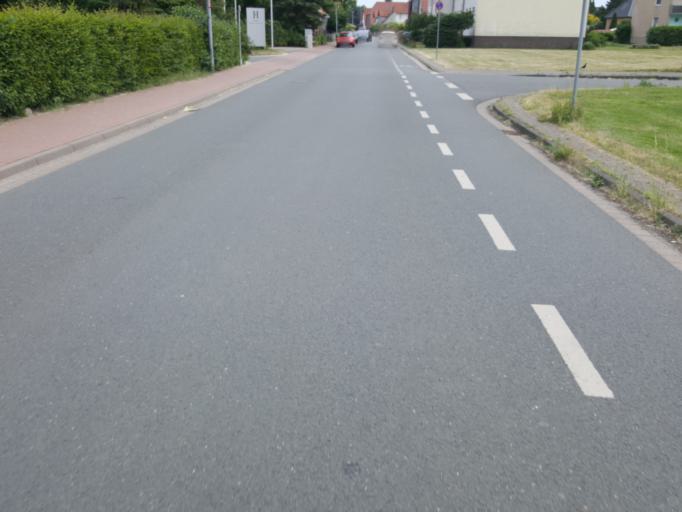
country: DE
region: Lower Saxony
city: Stolzenau
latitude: 52.5156
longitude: 9.0674
